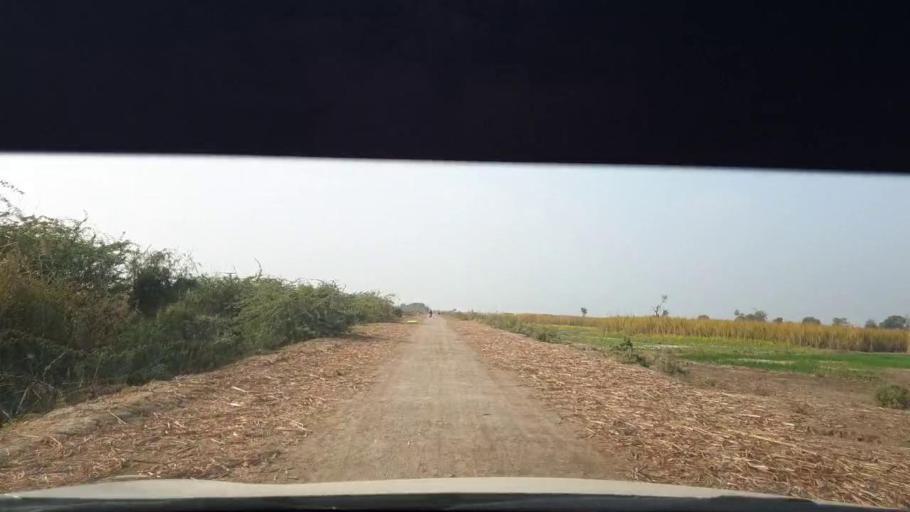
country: PK
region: Sindh
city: Berani
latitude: 25.7455
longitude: 68.9486
